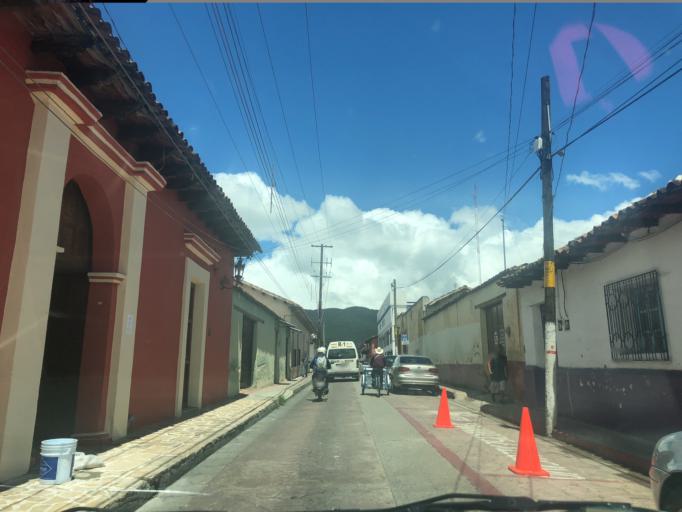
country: MX
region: Chiapas
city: San Cristobal de las Casas
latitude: 16.7337
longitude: -92.6390
